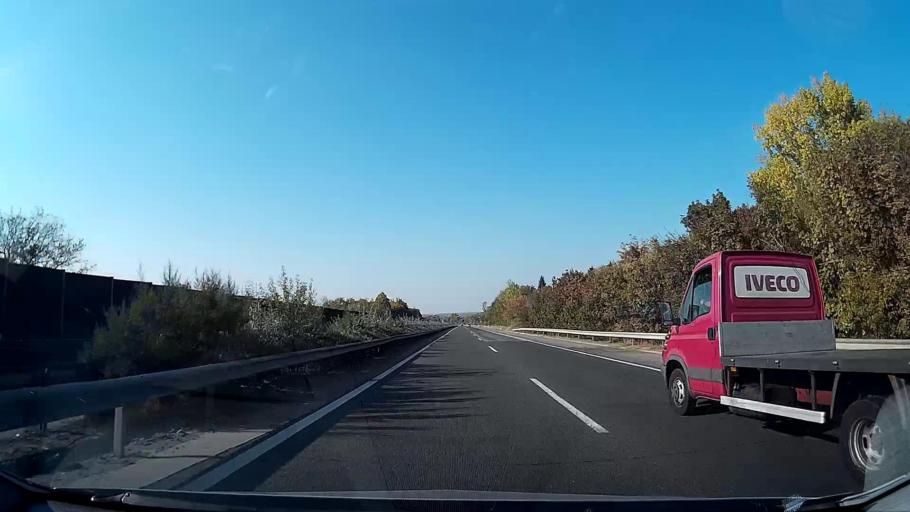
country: HU
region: Komarom-Esztergom
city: Tatabanya
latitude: 47.5884
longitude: 18.4026
